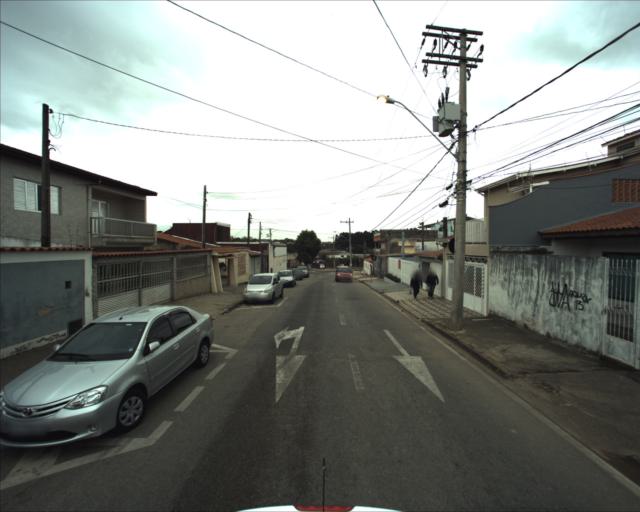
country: BR
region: Sao Paulo
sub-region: Sorocaba
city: Sorocaba
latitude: -23.4736
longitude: -47.4556
